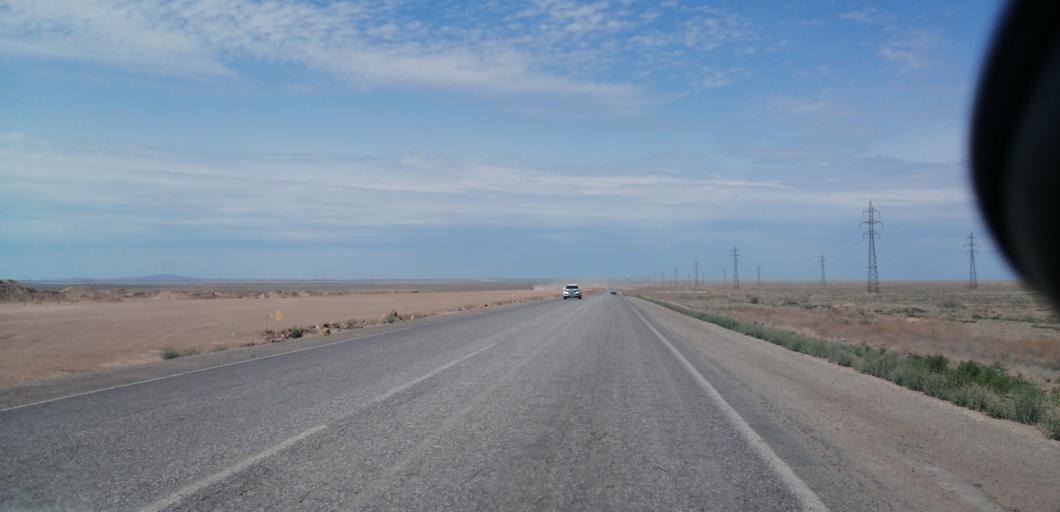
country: KZ
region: Qaraghandy
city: Balqash
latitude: 46.8048
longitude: 74.6990
